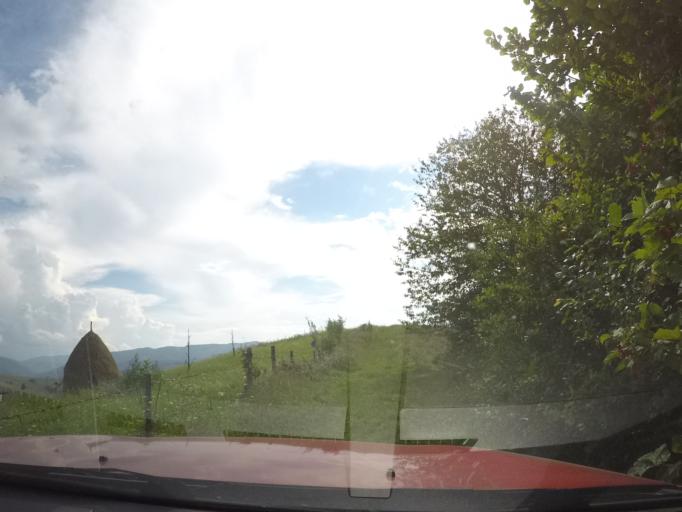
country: PL
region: Subcarpathian Voivodeship
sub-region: Powiat bieszczadzki
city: Lutowiska
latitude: 49.0307
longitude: 22.6437
